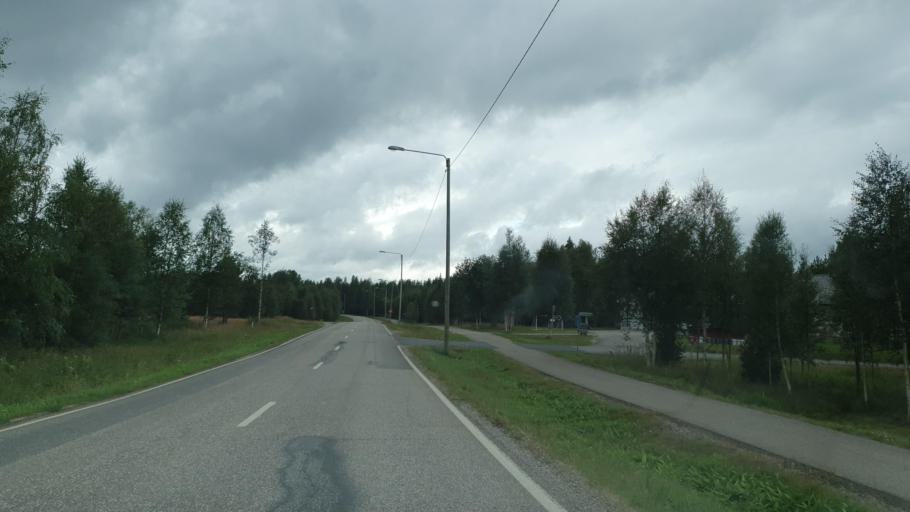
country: FI
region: Lapland
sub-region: Tunturi-Lappi
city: Kolari
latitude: 67.5219
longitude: 24.2918
